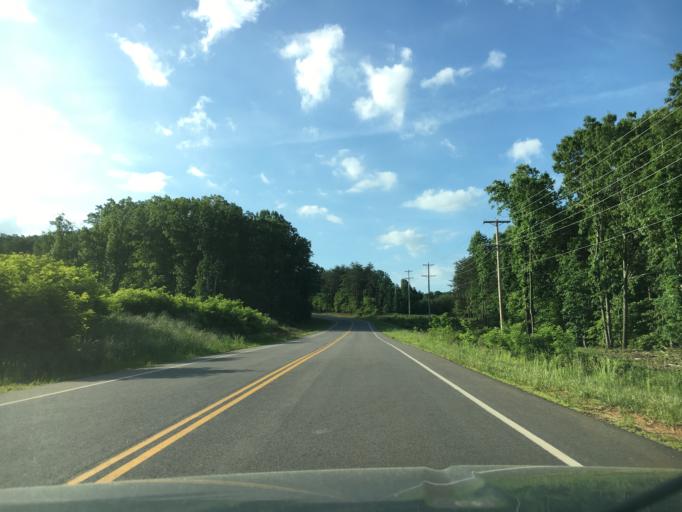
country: US
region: Virginia
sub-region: City of Lynchburg
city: West Lynchburg
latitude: 37.3367
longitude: -79.1869
